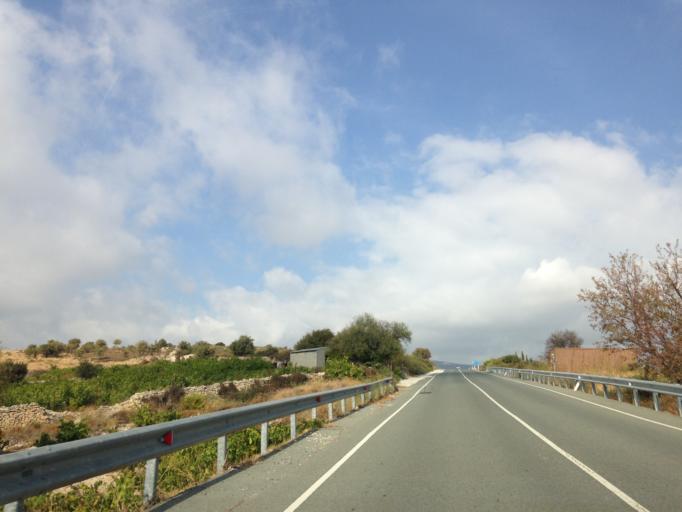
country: CY
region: Limassol
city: Pachna
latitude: 34.8161
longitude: 32.7942
